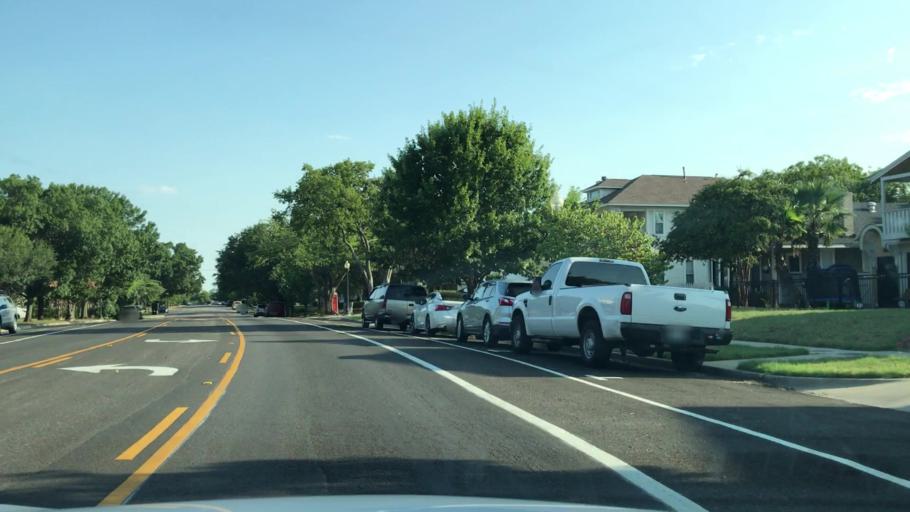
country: US
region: Texas
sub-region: Dallas County
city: Dallas
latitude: 32.7560
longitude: -96.8279
